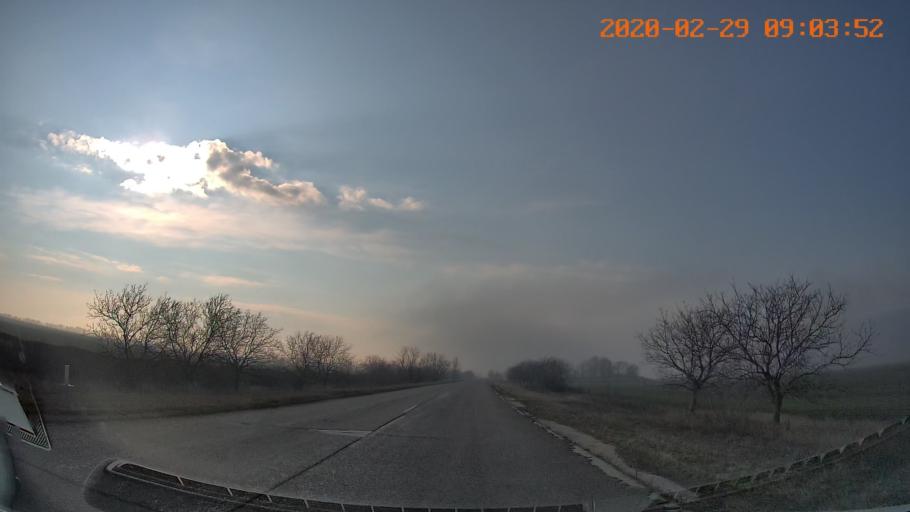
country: UA
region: Odessa
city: Velykoploske
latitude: 46.9108
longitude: 29.7334
